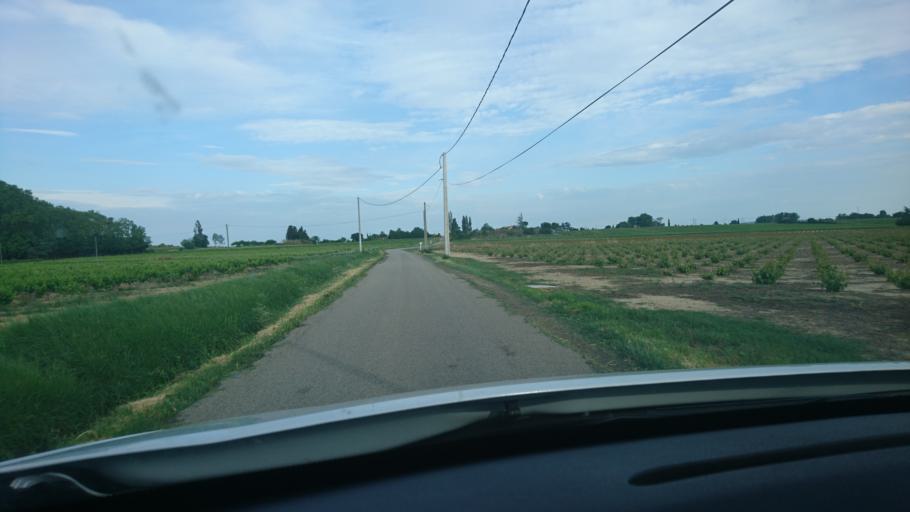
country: FR
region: Provence-Alpes-Cote d'Azur
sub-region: Departement du Vaucluse
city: Jonquieres
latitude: 44.1334
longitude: 4.8830
